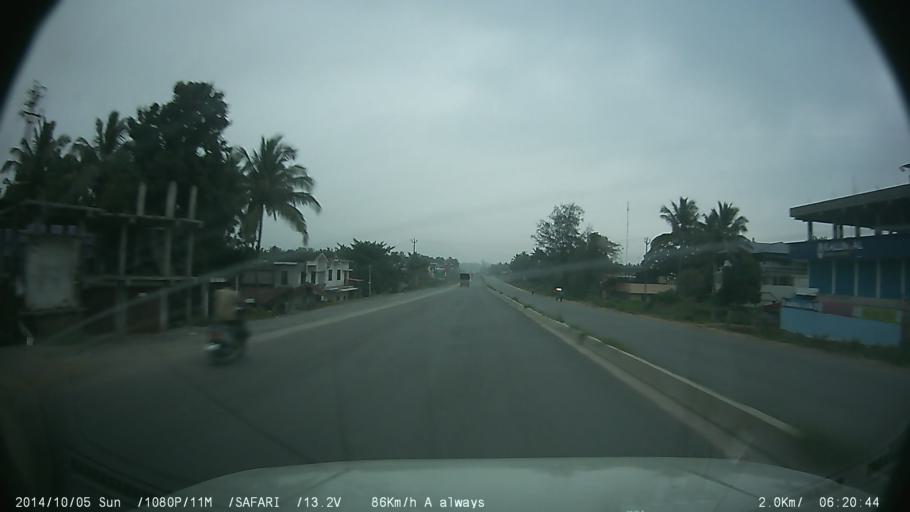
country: IN
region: Kerala
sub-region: Palakkad district
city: Palakkad
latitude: 10.7794
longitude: 76.7126
